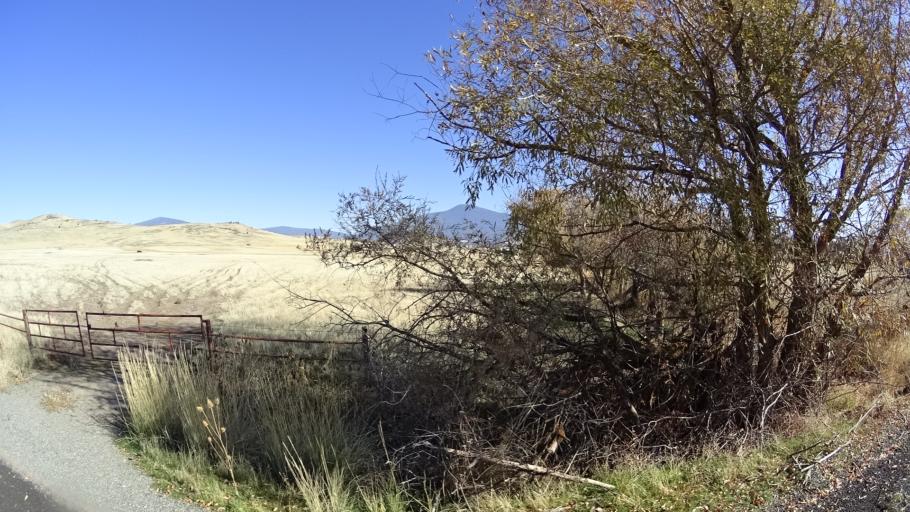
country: US
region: California
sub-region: Siskiyou County
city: Montague
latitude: 41.7276
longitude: -122.3988
